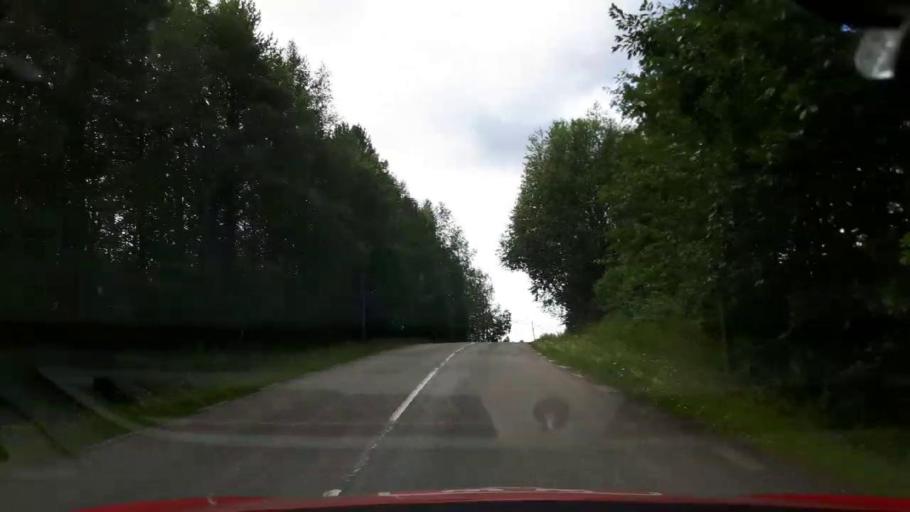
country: SE
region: Jaemtland
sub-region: Harjedalens Kommun
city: Sveg
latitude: 61.8468
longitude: 14.0516
